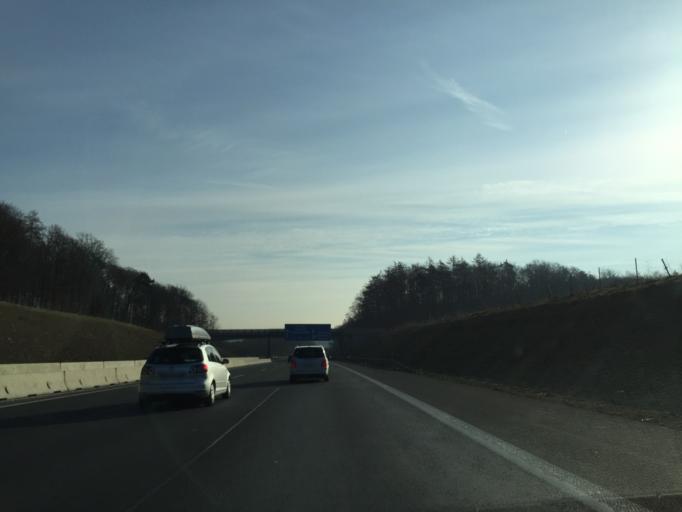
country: DE
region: Bavaria
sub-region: Regierungsbezirk Unterfranken
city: Uettingen
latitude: 49.7703
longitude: 9.7573
